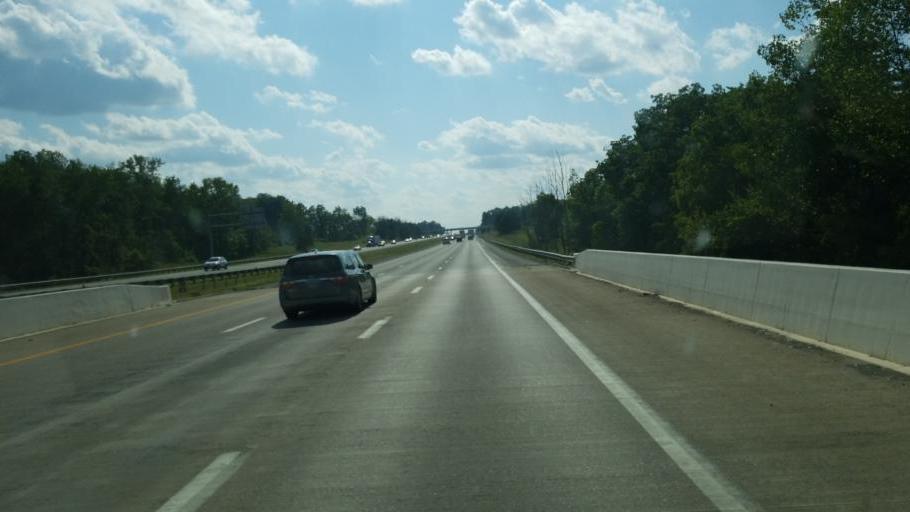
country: US
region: Ohio
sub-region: Medina County
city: Westfield Center
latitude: 41.0140
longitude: -81.9337
